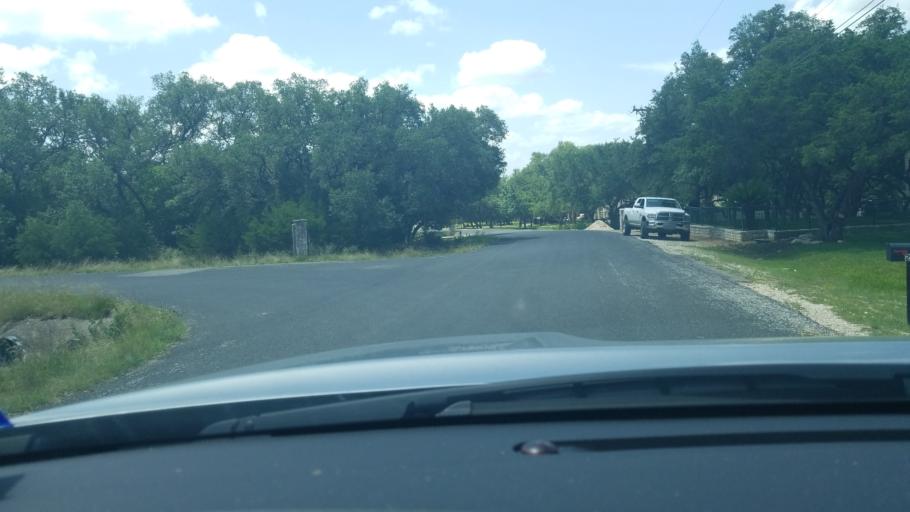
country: US
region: Texas
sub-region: Bexar County
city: Timberwood Park
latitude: 29.6919
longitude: -98.4890
